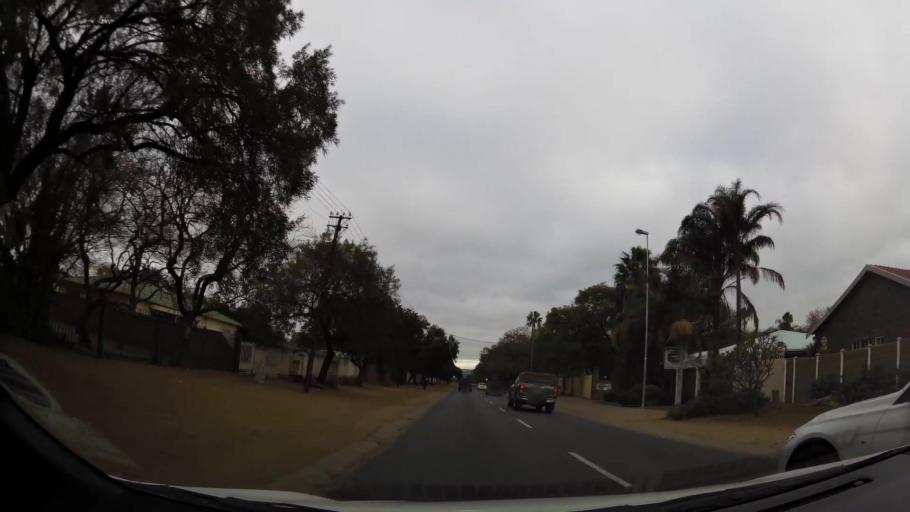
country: ZA
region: Limpopo
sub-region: Capricorn District Municipality
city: Polokwane
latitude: -23.9035
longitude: 29.4580
